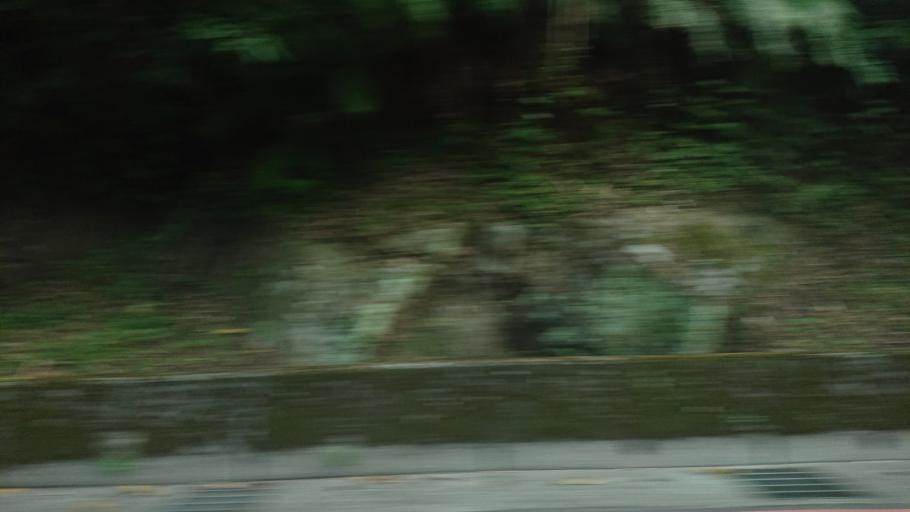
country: TW
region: Taiwan
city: Daxi
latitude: 24.8757
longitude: 121.3830
